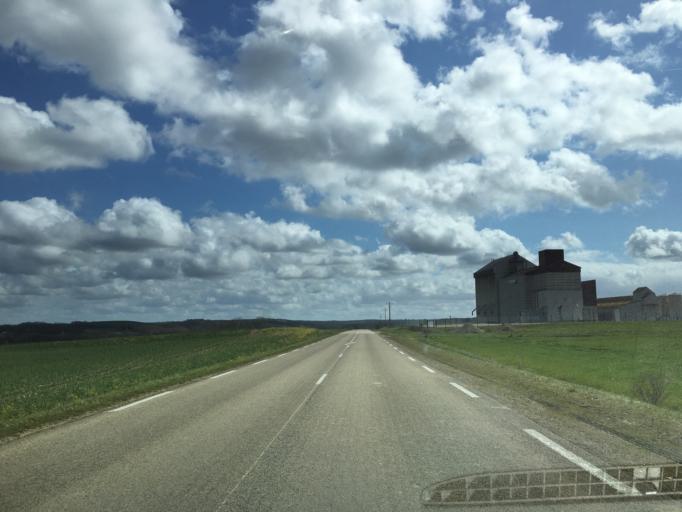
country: FR
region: Bourgogne
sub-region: Departement de l'Yonne
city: Aillant-sur-Tholon
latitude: 47.8516
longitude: 3.3786
